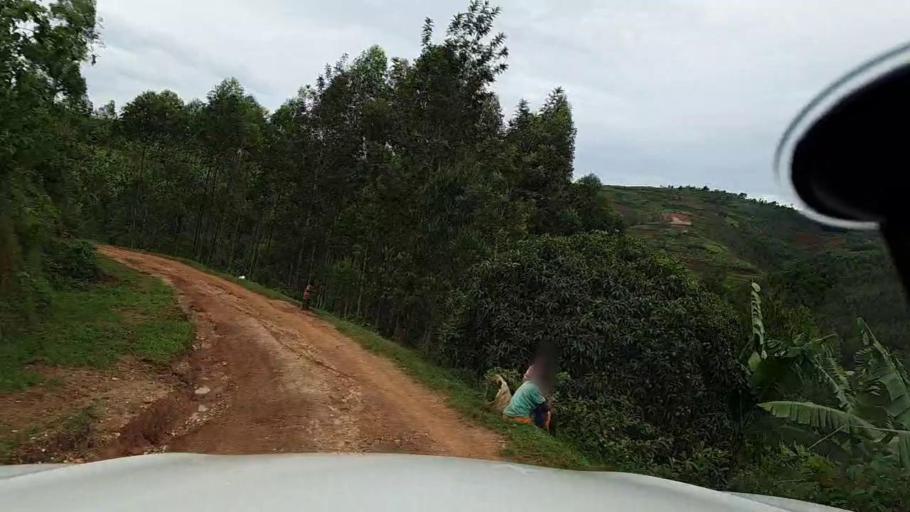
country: RW
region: Southern Province
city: Gitarama
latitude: -2.0915
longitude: 29.6384
